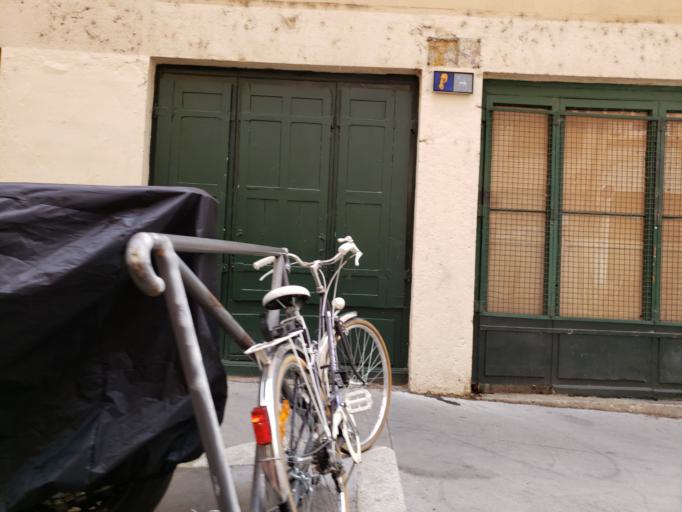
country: FR
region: Rhone-Alpes
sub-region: Departement du Rhone
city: Caluire-et-Cuire
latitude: 45.7721
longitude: 4.8271
